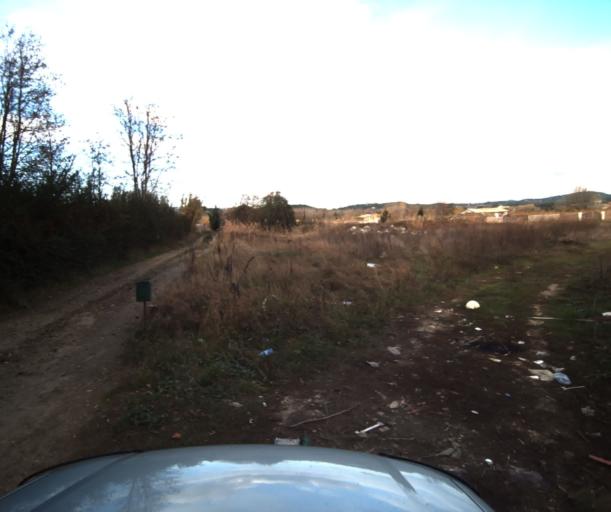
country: FR
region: Provence-Alpes-Cote d'Azur
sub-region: Departement du Vaucluse
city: Pertuis
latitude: 43.6707
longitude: 5.5187
